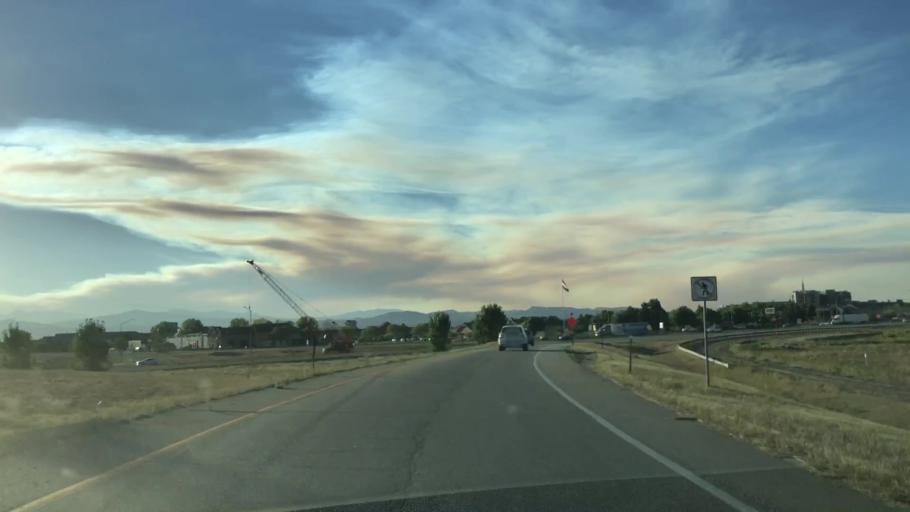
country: US
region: Colorado
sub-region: Larimer County
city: Loveland
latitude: 40.4075
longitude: -104.9908
